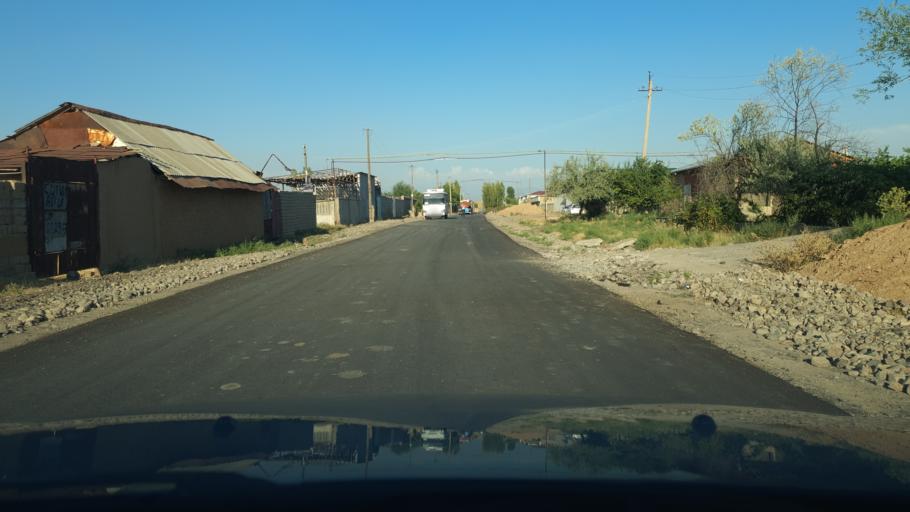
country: UZ
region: Toshkent
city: Salor
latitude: 41.4566
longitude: 69.4013
